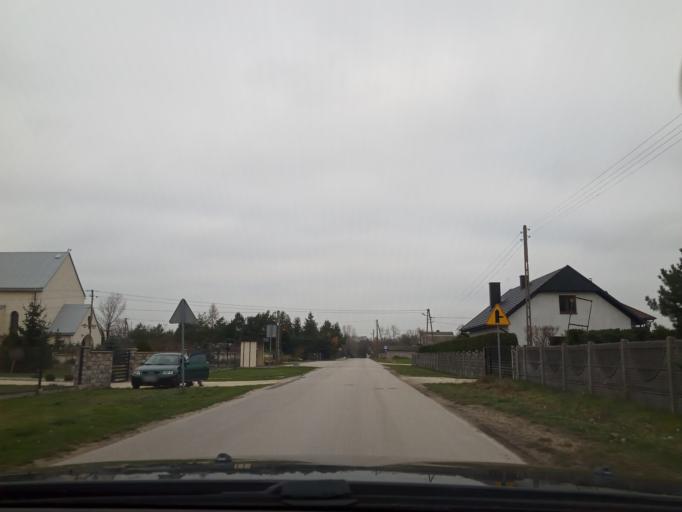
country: PL
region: Swietokrzyskie
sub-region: Powiat jedrzejowski
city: Imielno
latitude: 50.6000
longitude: 20.4852
